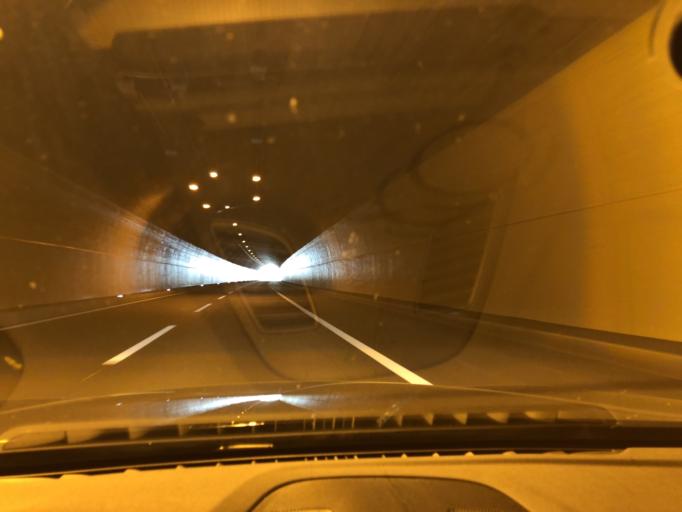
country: AT
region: Tyrol
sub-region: Politischer Bezirk Landeck
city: Flirsch
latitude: 47.1435
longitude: 10.3433
